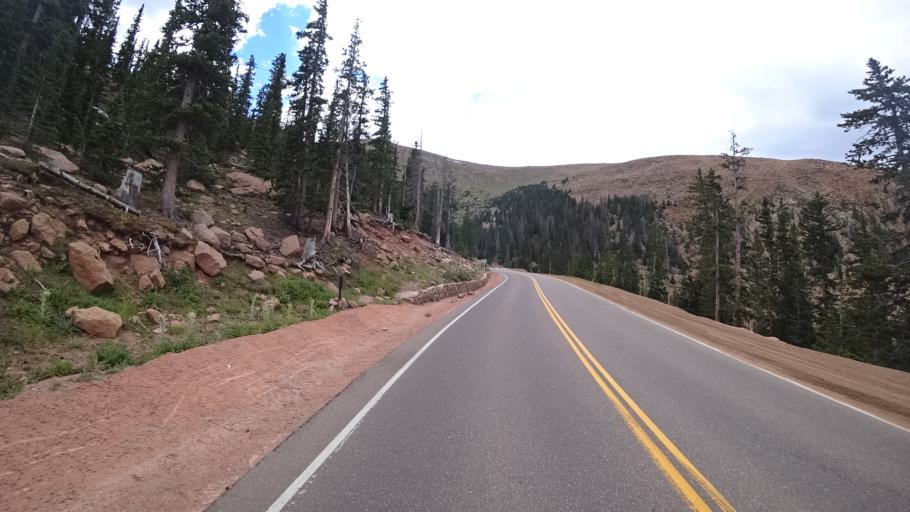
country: US
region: Colorado
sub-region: El Paso County
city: Cascade-Chipita Park
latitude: 38.8741
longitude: -105.0735
